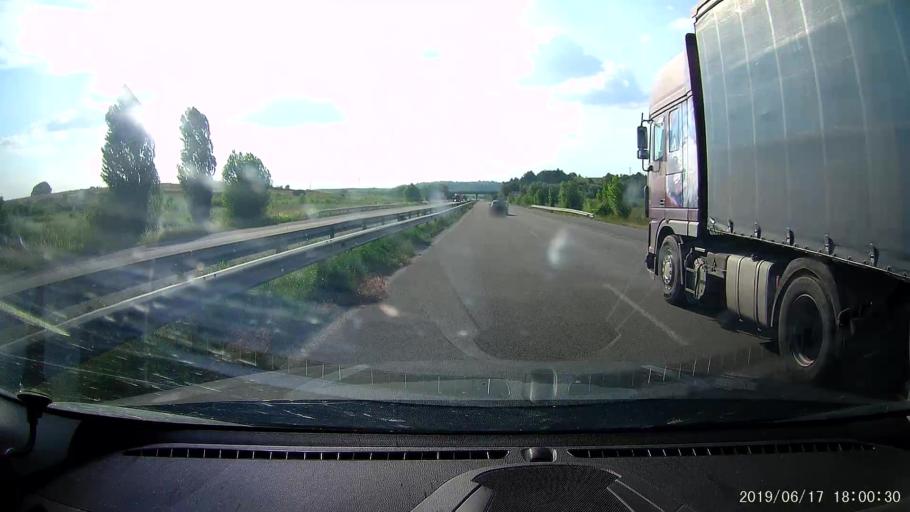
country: BG
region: Khaskovo
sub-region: Obshtina Svilengrad
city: Svilengrad
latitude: 41.7373
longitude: 26.2780
